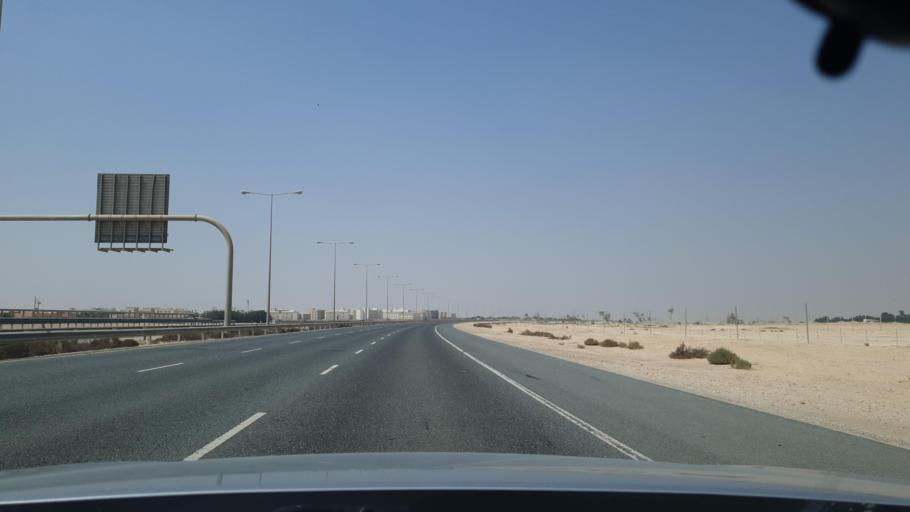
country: QA
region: Al Khawr
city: Al Khawr
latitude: 25.7555
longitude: 51.4318
